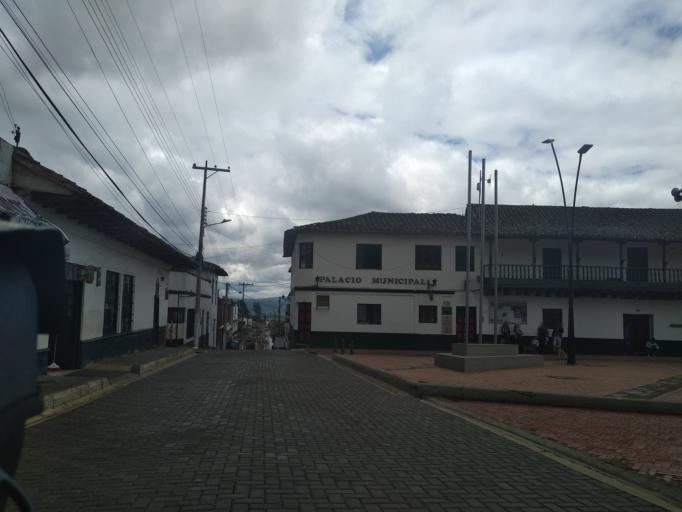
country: CO
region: Boyaca
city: Sotaquira
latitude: 5.7658
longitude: -73.2476
